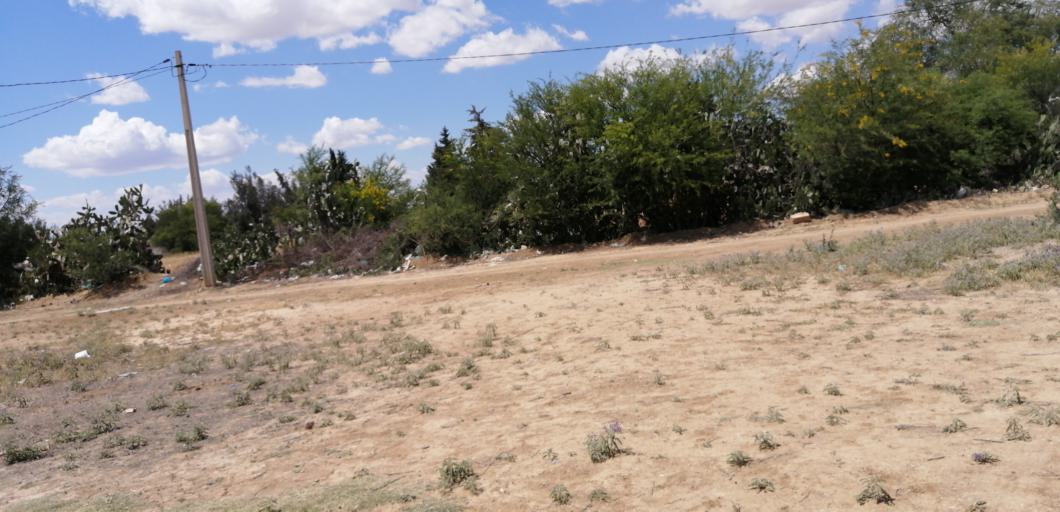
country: TN
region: Al Qayrawan
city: Kairouan
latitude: 35.6171
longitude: 9.9225
